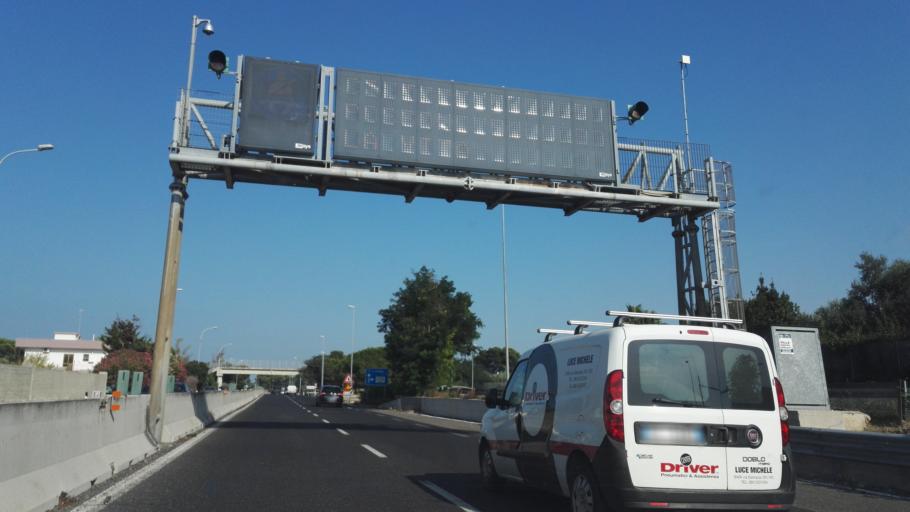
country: IT
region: Apulia
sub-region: Provincia di Bari
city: Parco Scizzo-Parchitello
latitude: 41.0883
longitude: 16.9820
